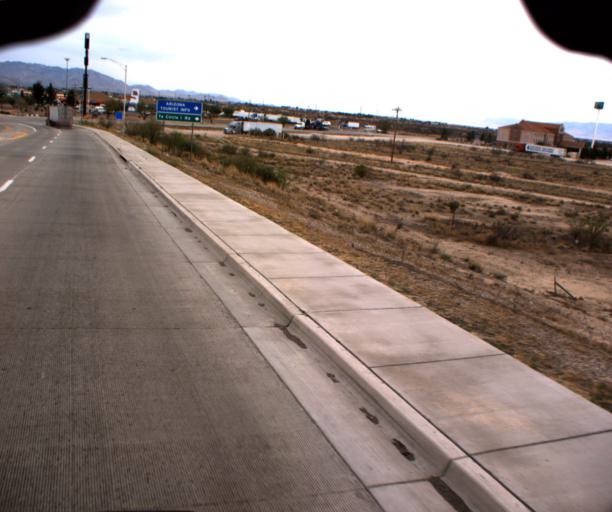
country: US
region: Arizona
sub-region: Cochise County
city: Willcox
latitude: 32.2671
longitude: -109.8449
